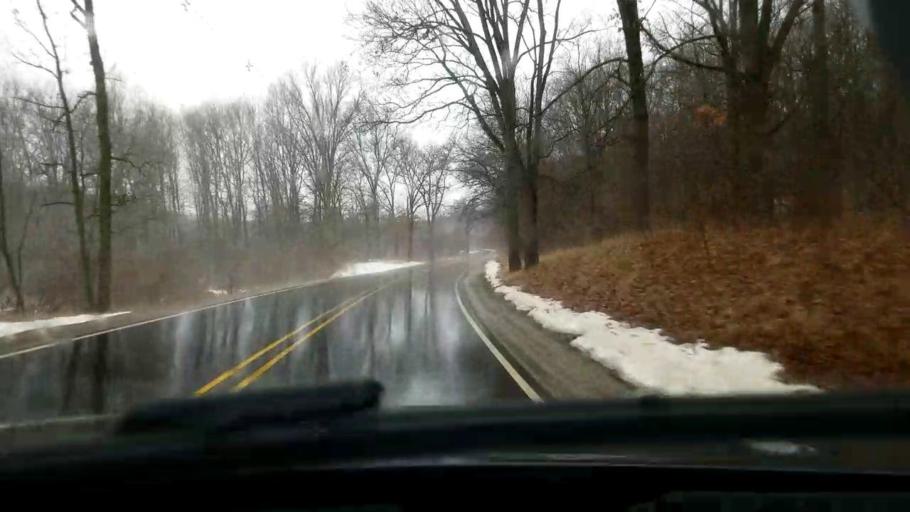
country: US
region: Michigan
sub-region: Jackson County
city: Grass Lake
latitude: 42.3243
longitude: -84.2141
